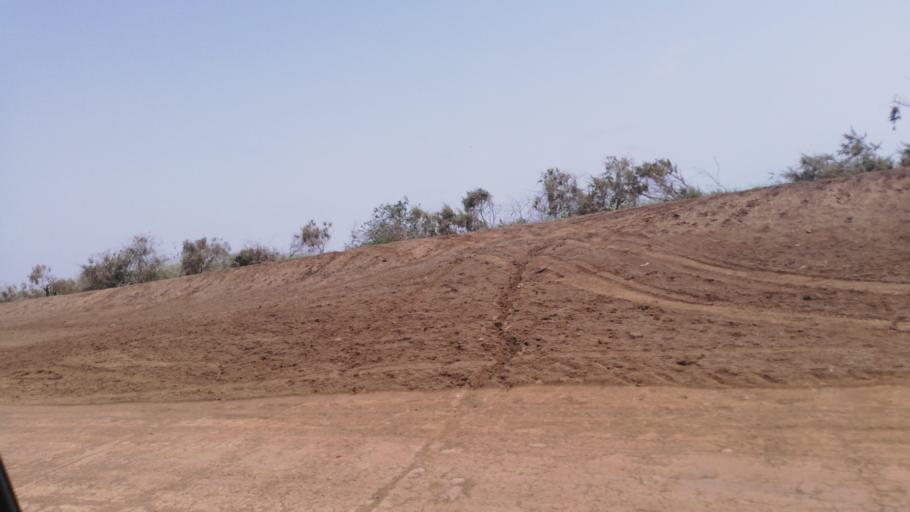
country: SN
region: Saint-Louis
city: Saint-Louis
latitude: 16.4028
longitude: -16.2927
